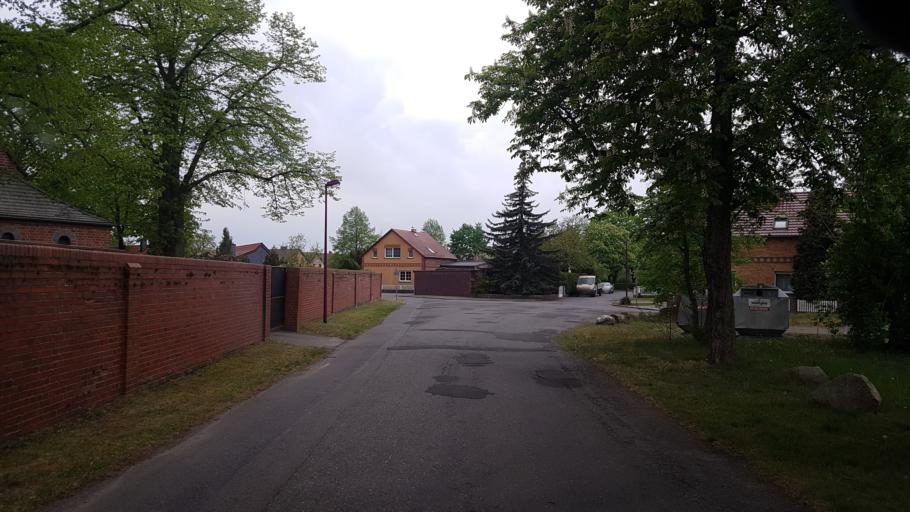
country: DE
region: Brandenburg
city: Grossraschen
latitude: 51.5844
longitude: 13.9633
